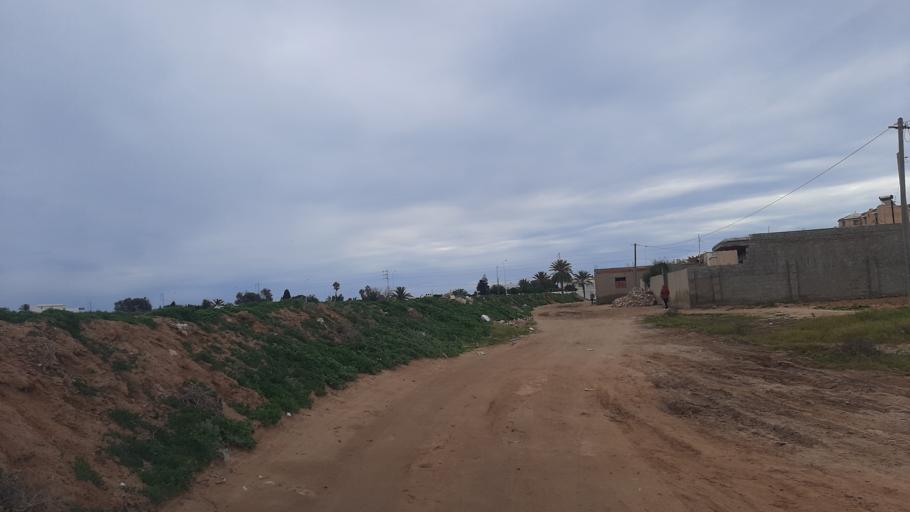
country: TN
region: Safaqis
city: Al Qarmadah
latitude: 34.7975
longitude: 10.8559
